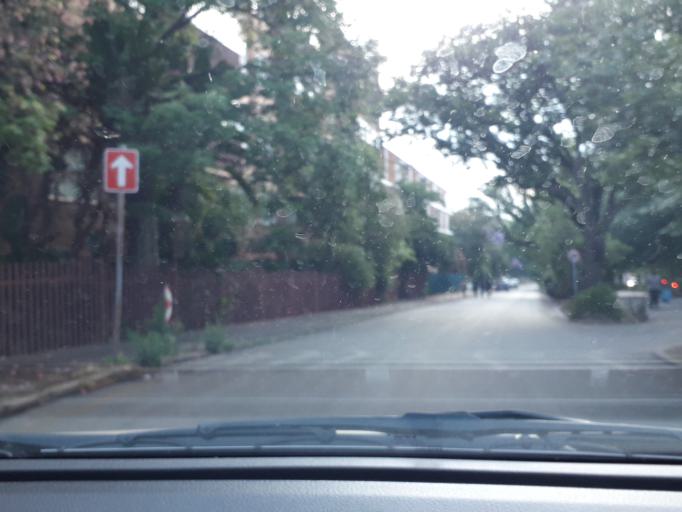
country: ZA
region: Gauteng
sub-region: City of Johannesburg Metropolitan Municipality
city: Johannesburg
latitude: -26.1837
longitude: 28.0459
